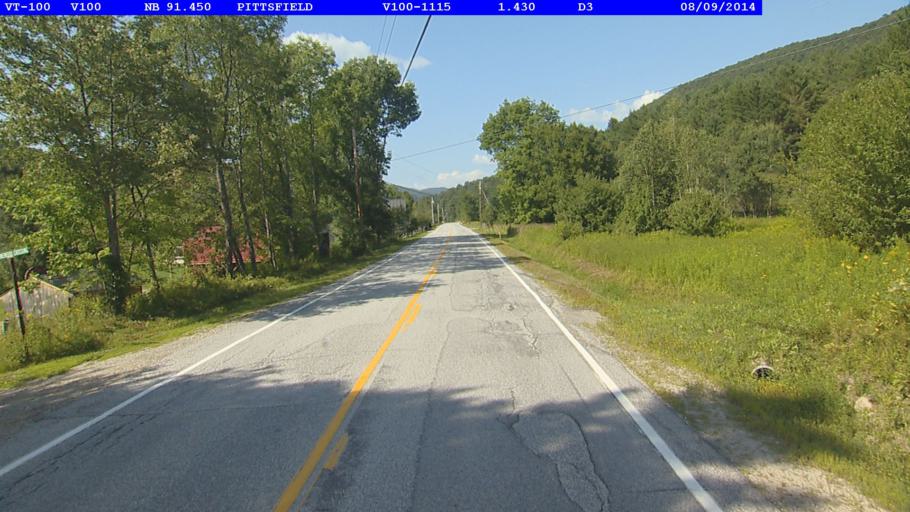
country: US
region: Vermont
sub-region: Rutland County
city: Rutland
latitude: 43.7376
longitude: -72.8204
